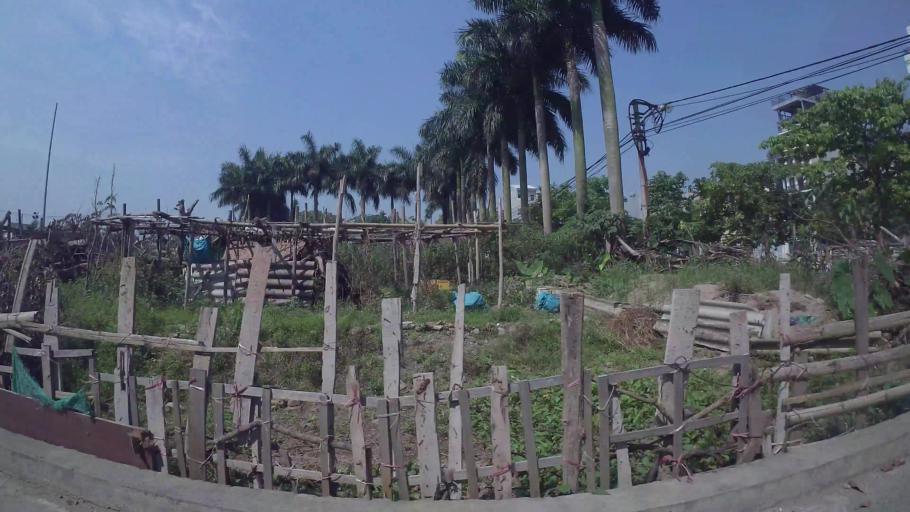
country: VN
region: Ha Noi
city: Hoan Kiem
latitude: 21.0629
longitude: 105.8698
